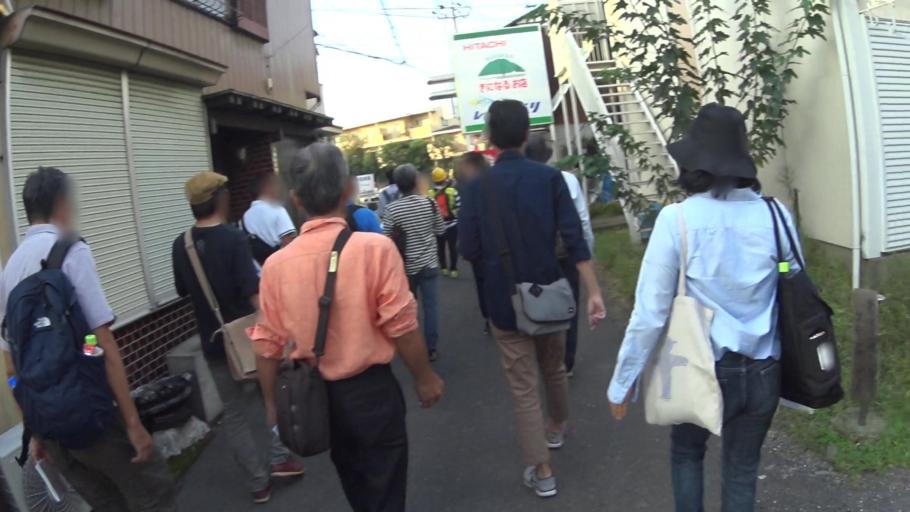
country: JP
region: Tokyo
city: Tanashicho
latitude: 35.7555
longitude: 139.5447
